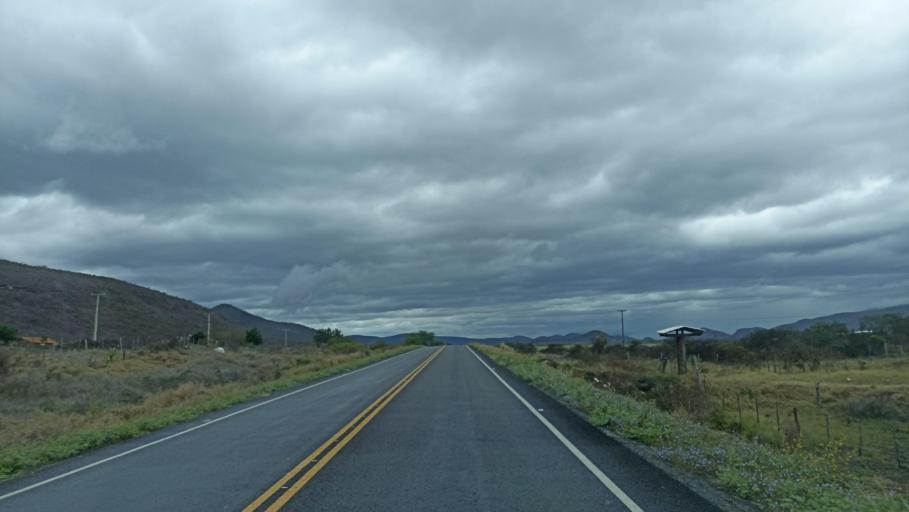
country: BR
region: Bahia
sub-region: Iacu
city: Iacu
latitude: -12.8805
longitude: -40.3902
